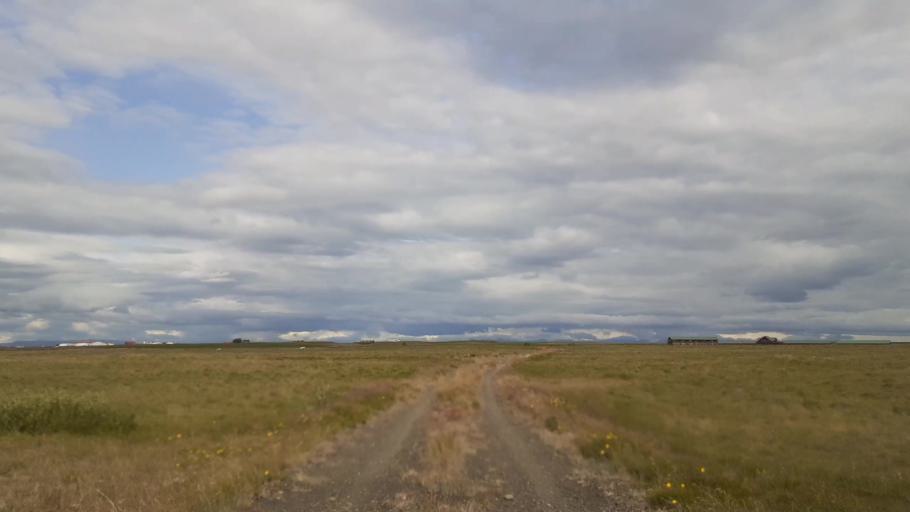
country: IS
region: South
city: Vestmannaeyjar
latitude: 63.7747
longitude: -20.2998
